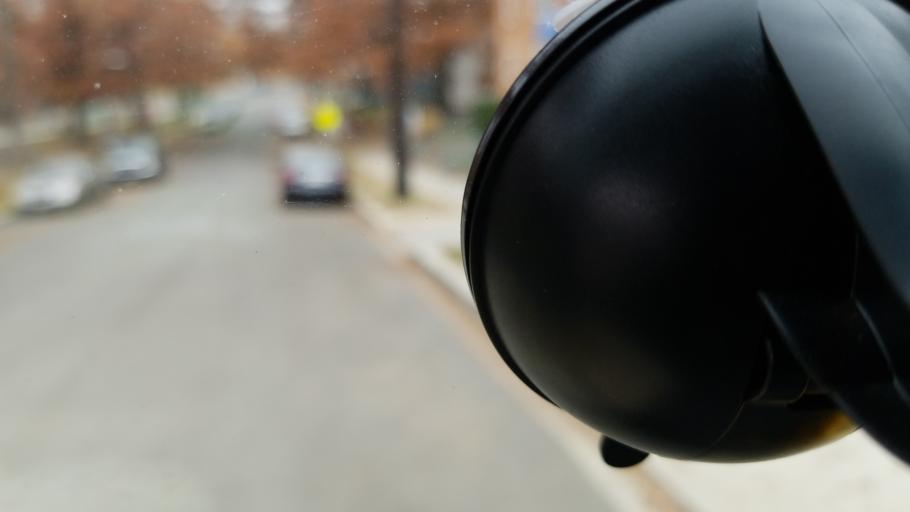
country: US
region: Maryland
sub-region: Prince George's County
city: Coral Hills
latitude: 38.8863
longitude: -76.9546
